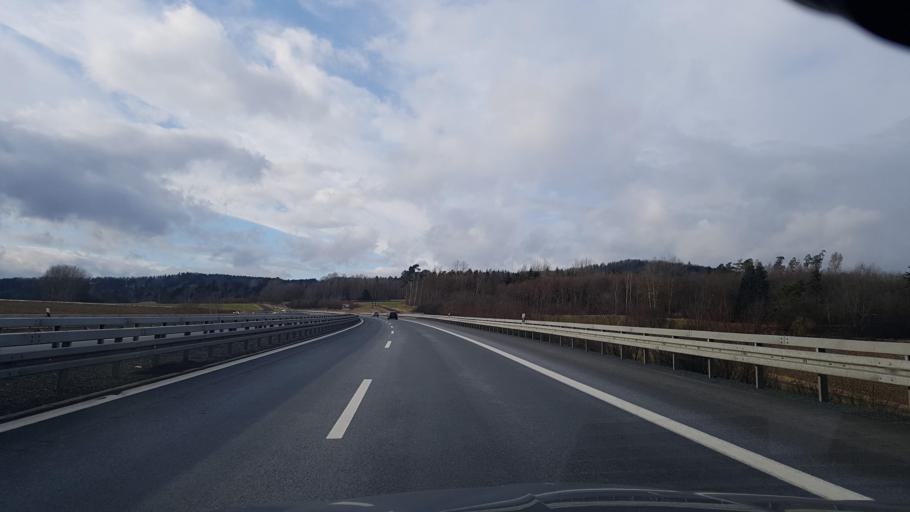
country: DE
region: Bavaria
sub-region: Upper Palatinate
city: Pechbrunn
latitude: 49.9781
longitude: 12.1700
